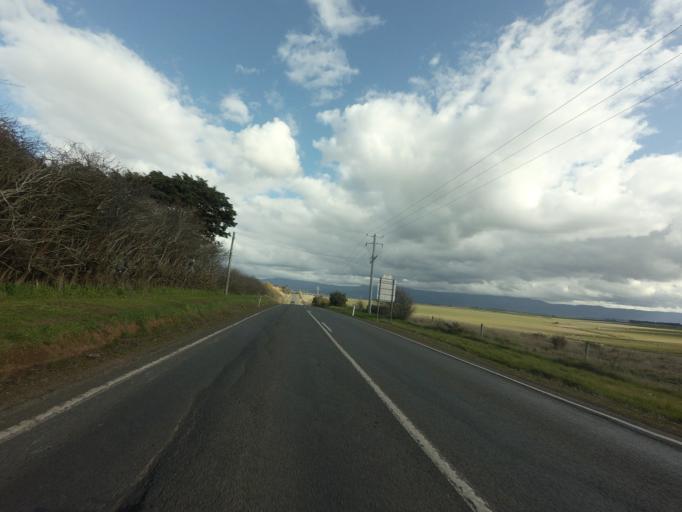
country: AU
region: Tasmania
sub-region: Northern Midlands
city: Longford
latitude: -41.6967
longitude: 147.0780
